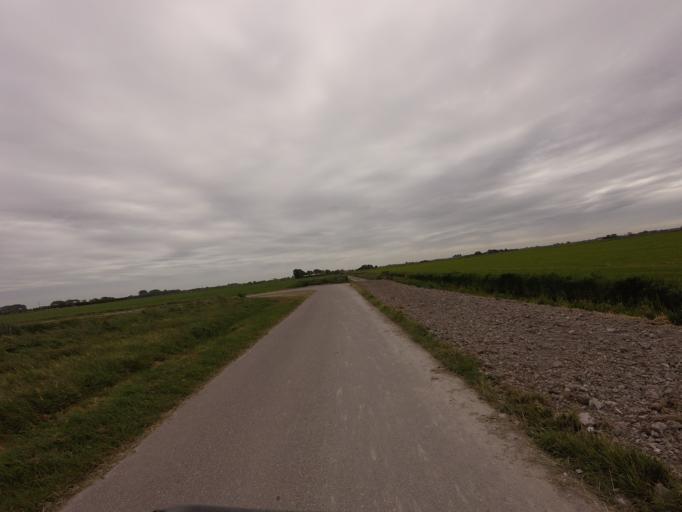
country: NL
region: North Holland
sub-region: Gemeente Medemblik
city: Opperdoes
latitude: 52.7318
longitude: 5.0567
